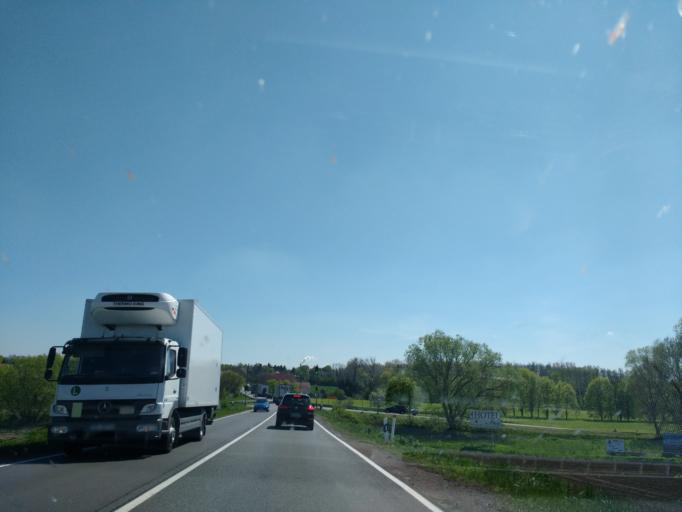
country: DE
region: Saxony-Anhalt
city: Deuben
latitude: 51.1326
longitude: 12.0541
